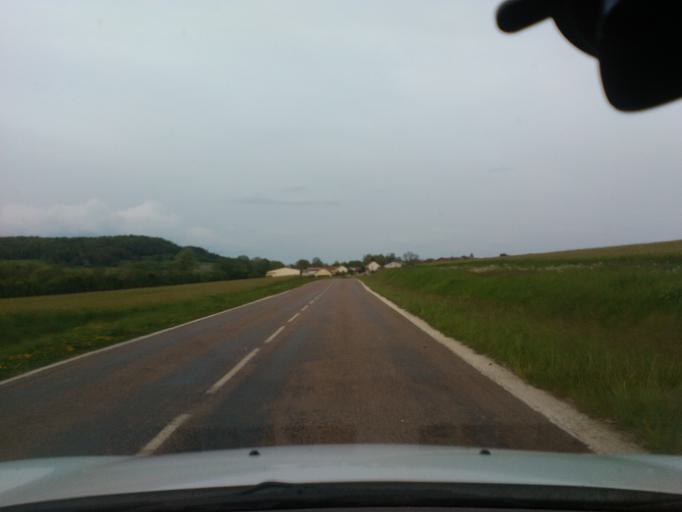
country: FR
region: Champagne-Ardenne
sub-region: Departement de la Haute-Marne
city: Bologne
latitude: 48.2164
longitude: 5.2366
